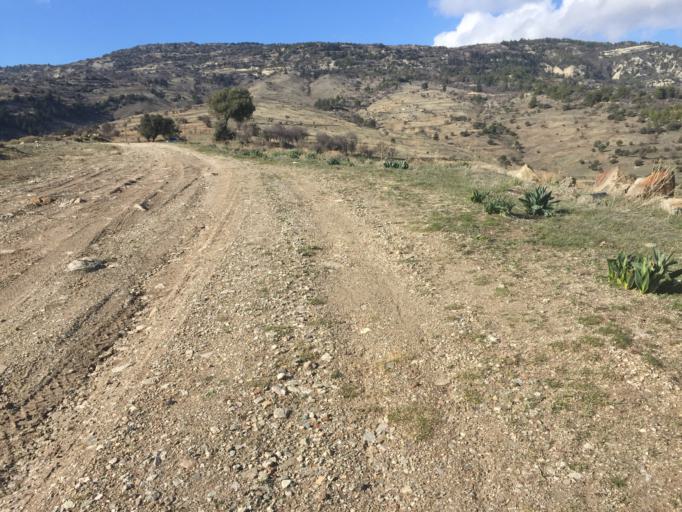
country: CY
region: Limassol
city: Pachna
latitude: 34.8854
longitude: 32.6538
